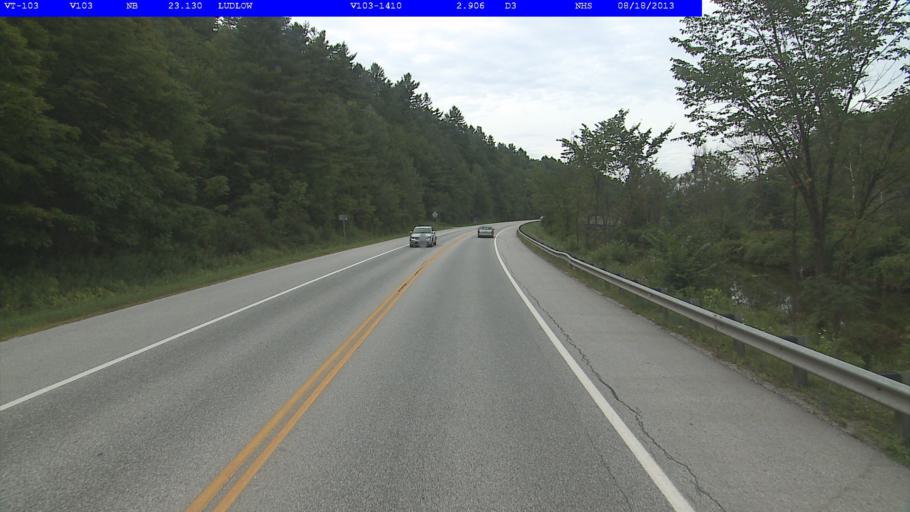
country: US
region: Vermont
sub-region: Windsor County
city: Chester
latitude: 43.4041
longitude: -72.7077
